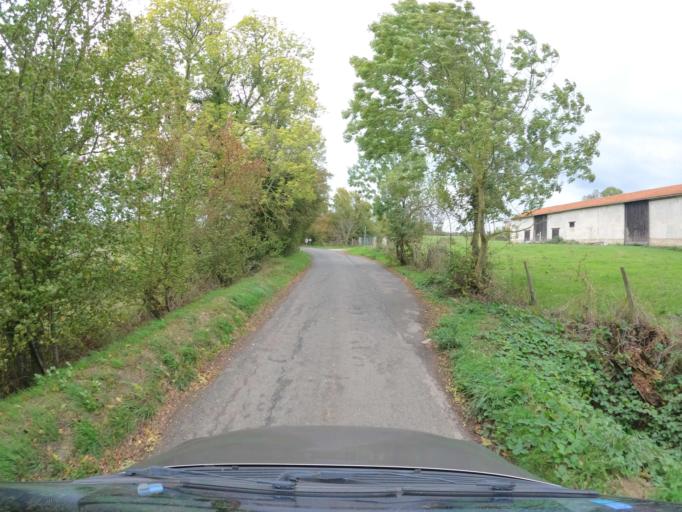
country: FR
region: Ile-de-France
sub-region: Departement de Seine-et-Marne
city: Montry
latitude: 48.8728
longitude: 2.8318
